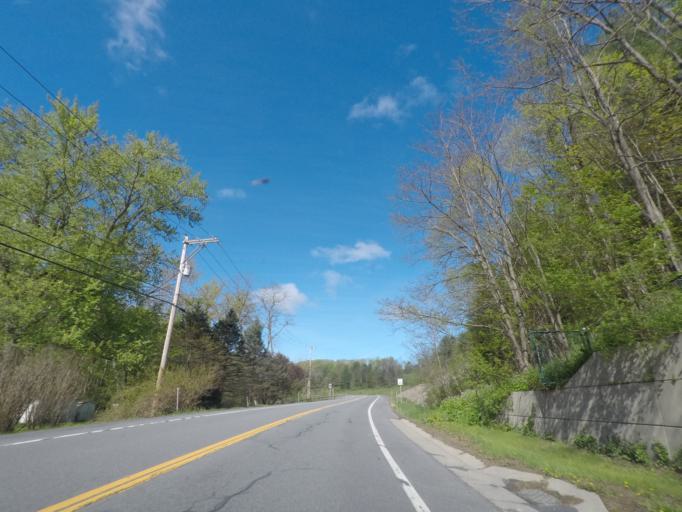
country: US
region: New York
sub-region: Albany County
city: Ravena
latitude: 42.4750
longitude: -73.9120
